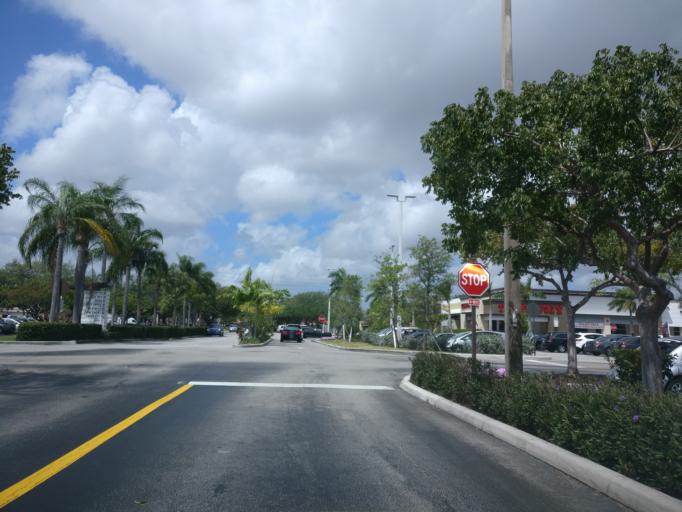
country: US
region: Florida
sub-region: Broward County
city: Pine Island Ridge
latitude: 26.0924
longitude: -80.2489
